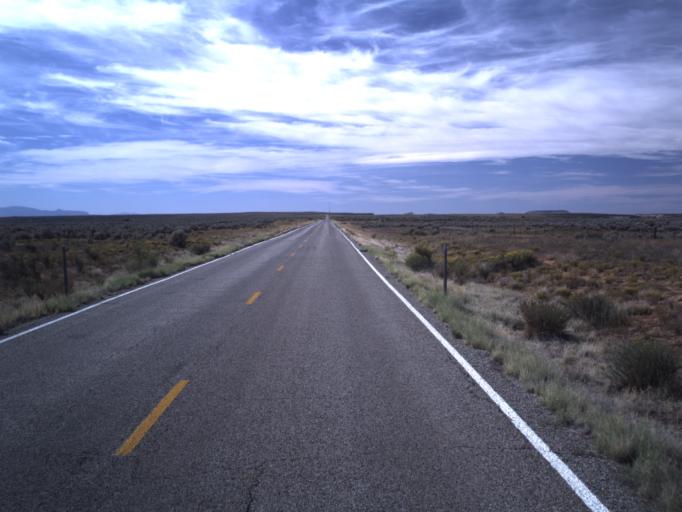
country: US
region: Utah
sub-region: San Juan County
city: Blanding
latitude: 37.3881
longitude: -109.3400
